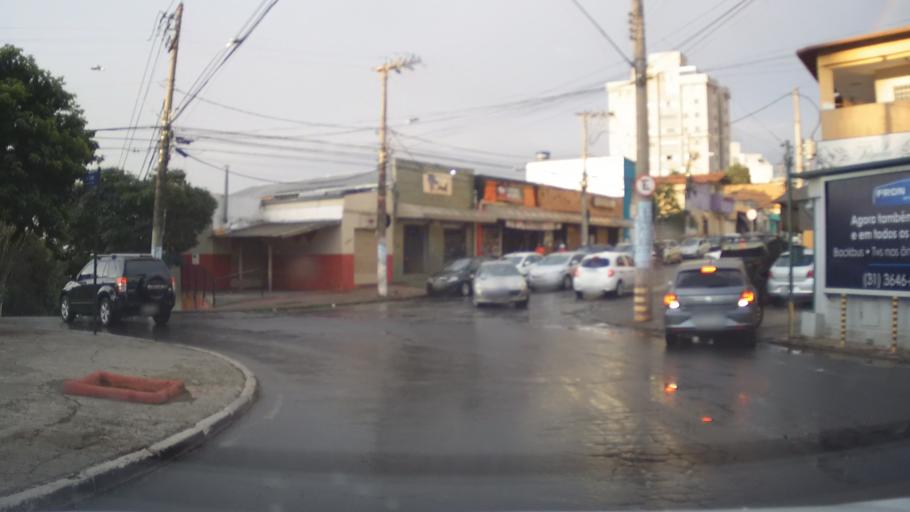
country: BR
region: Minas Gerais
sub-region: Belo Horizonte
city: Belo Horizonte
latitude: -19.9656
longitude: -43.9818
